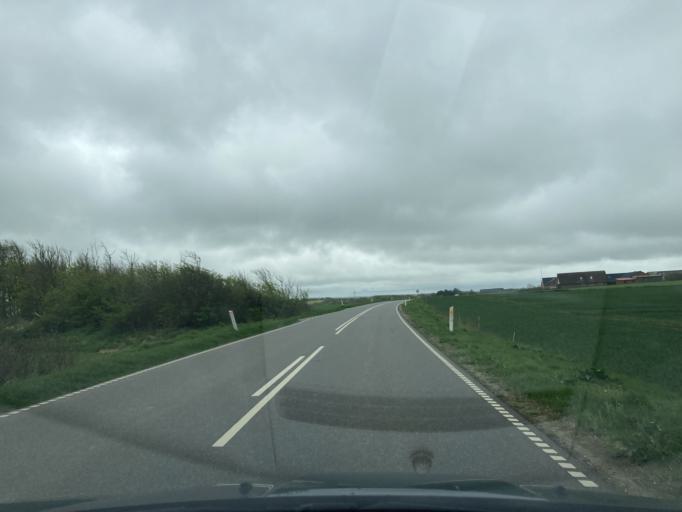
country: DK
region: North Denmark
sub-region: Thisted Kommune
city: Hurup
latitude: 56.8305
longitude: 8.3596
